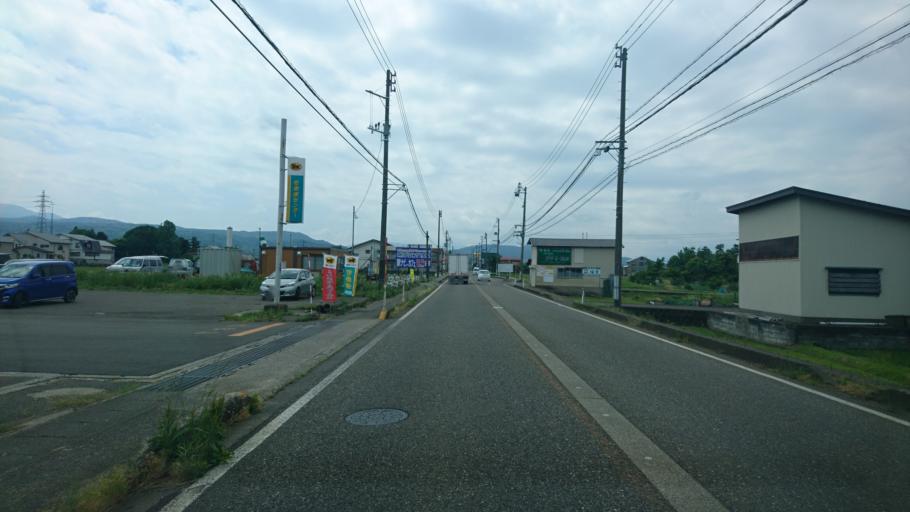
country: JP
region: Niigata
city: Arai
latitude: 37.0488
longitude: 138.2607
